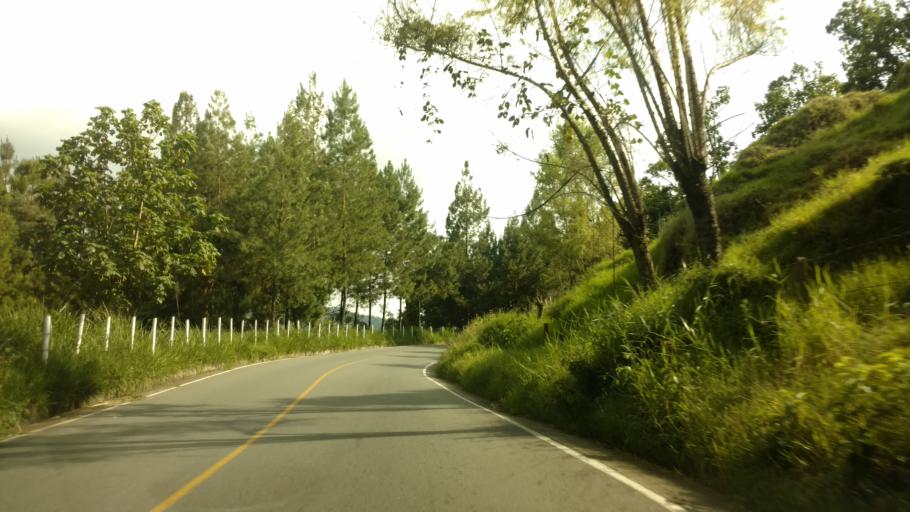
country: CO
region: Caldas
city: Neira
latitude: 5.1460
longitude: -75.5075
